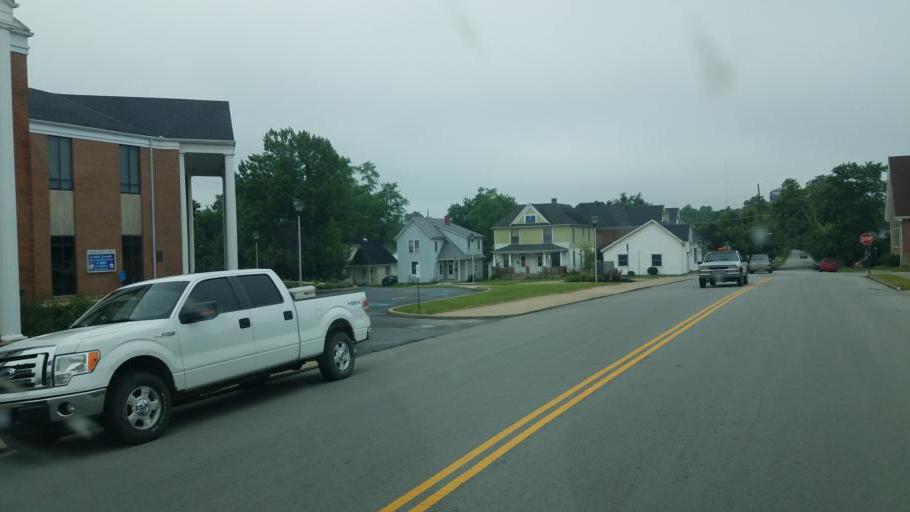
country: US
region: Ohio
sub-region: Highland County
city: Hillsboro
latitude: 39.2012
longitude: -83.6135
